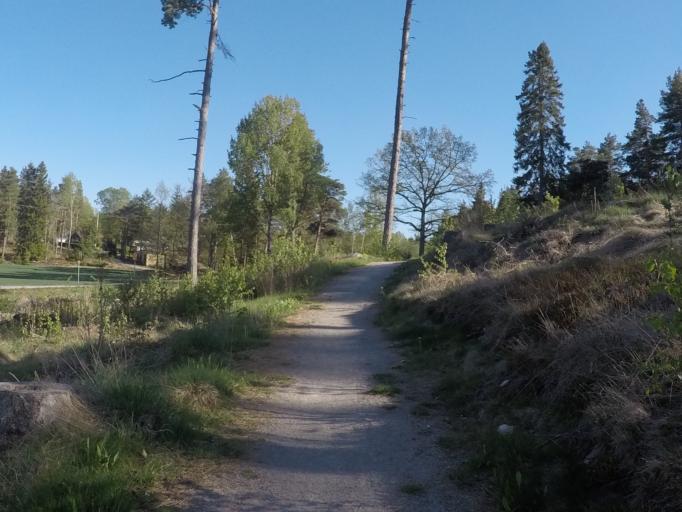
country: SE
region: Soedermanland
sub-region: Eskilstuna Kommun
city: Eskilstuna
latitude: 59.3998
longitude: 16.5482
